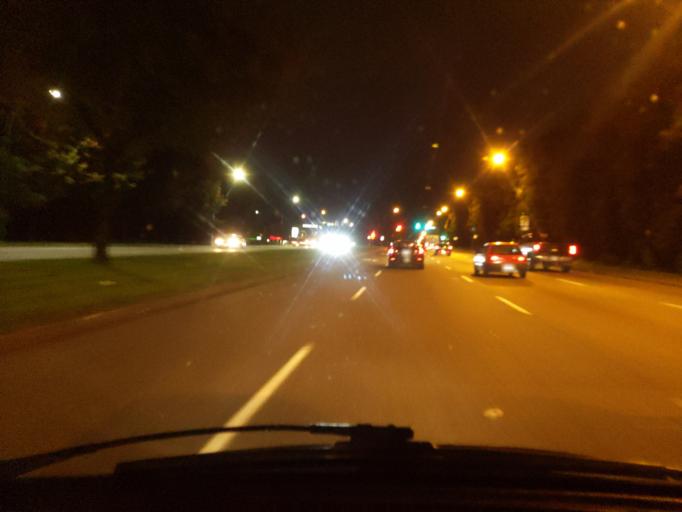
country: CA
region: British Columbia
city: Burnaby
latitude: 49.2562
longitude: -123.0238
